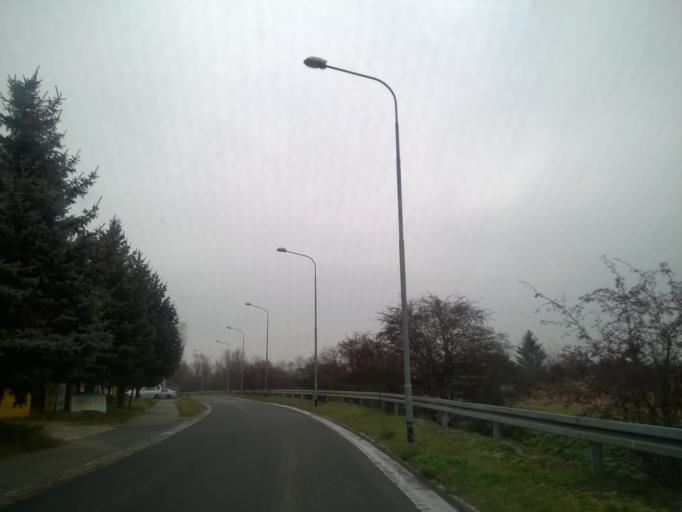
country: PL
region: Lower Silesian Voivodeship
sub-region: Powiat wroclawski
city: Wroclaw
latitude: 51.0697
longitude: 17.0508
